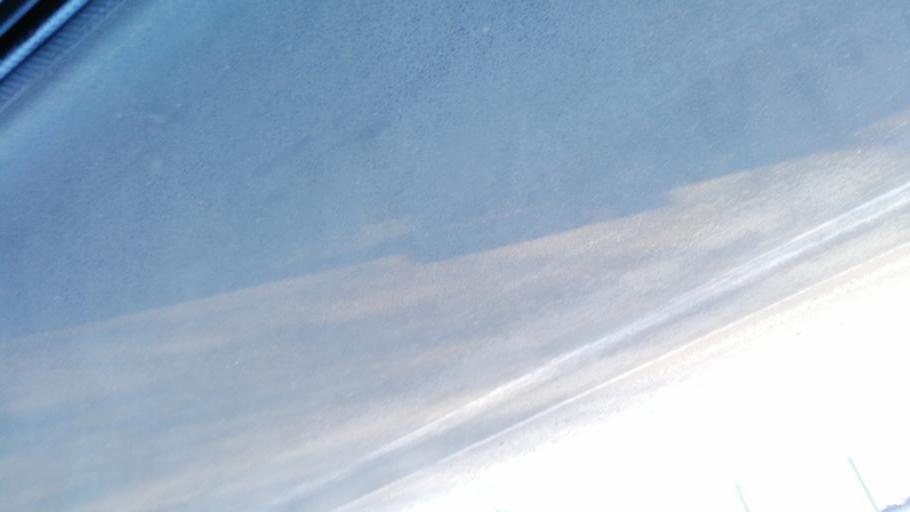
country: KZ
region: Aqtoebe
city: Aqtobe
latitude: 50.2853
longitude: 57.2120
